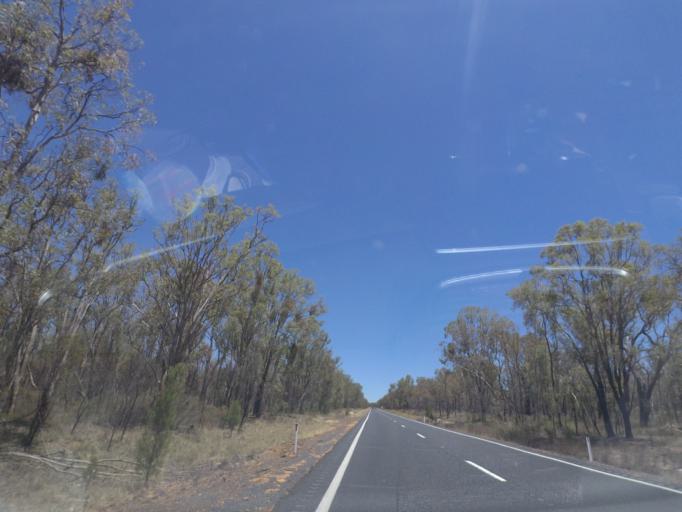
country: AU
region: New South Wales
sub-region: Warrumbungle Shire
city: Coonabarabran
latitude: -31.1676
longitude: 149.3631
